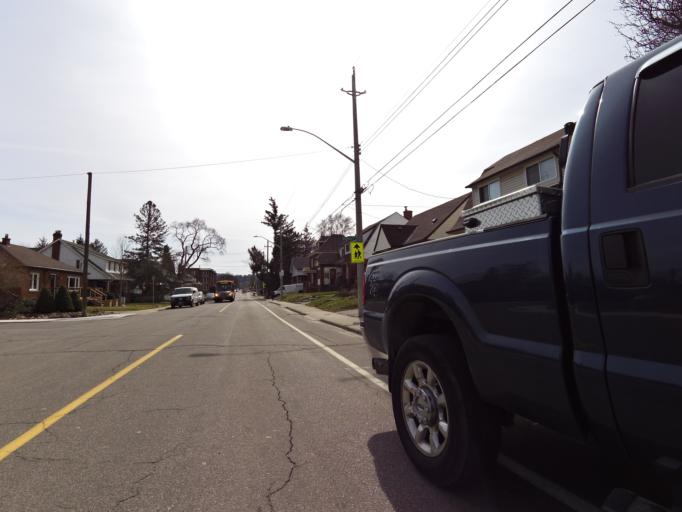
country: CA
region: Ontario
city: Hamilton
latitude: 43.2646
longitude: -79.9001
